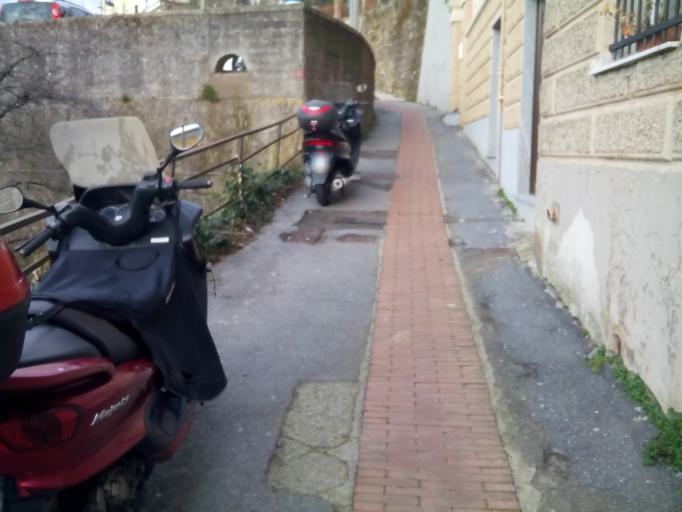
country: IT
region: Liguria
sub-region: Provincia di Genova
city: Piccarello
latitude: 44.4609
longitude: 8.9847
